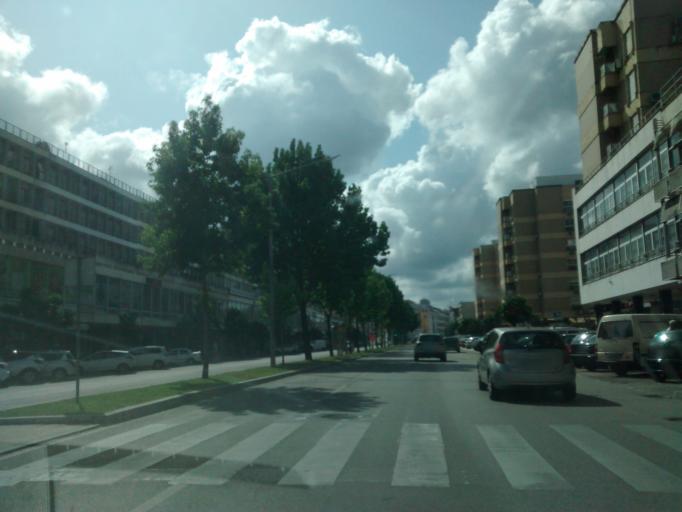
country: PT
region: Coimbra
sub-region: Coimbra
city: Coimbra
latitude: 40.2153
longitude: -8.4356
